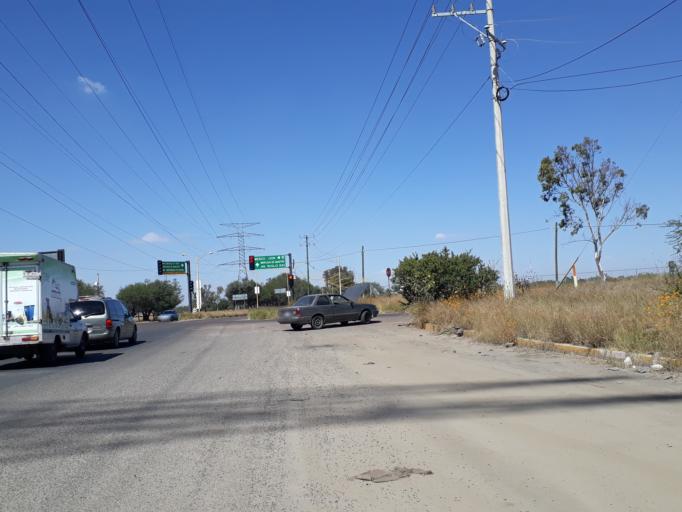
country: MX
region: Aguascalientes
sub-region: Aguascalientes
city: San Sebastian [Fraccionamiento]
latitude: 21.8208
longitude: -102.2939
